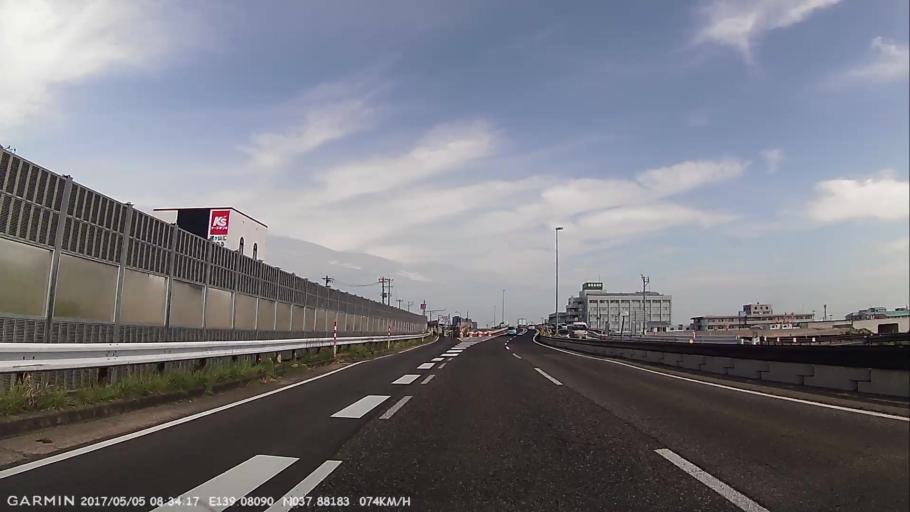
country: JP
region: Niigata
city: Kameda-honcho
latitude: 37.8820
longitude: 139.0807
